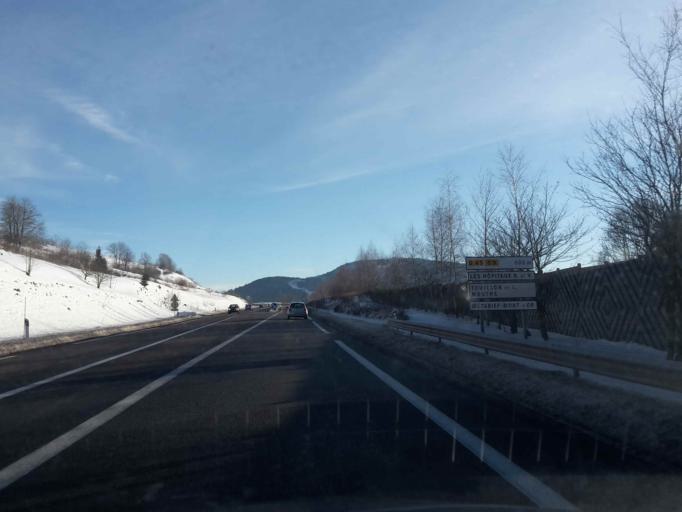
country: FR
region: Franche-Comte
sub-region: Departement du Doubs
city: Jougne
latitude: 46.7949
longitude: 6.3565
